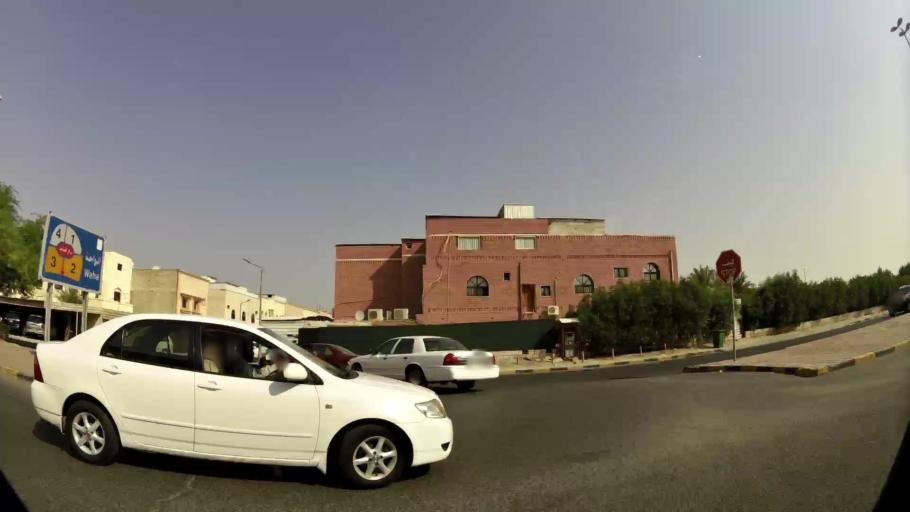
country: KW
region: Muhafazat al Jahra'
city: Al Jahra'
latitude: 29.3381
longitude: 47.6584
